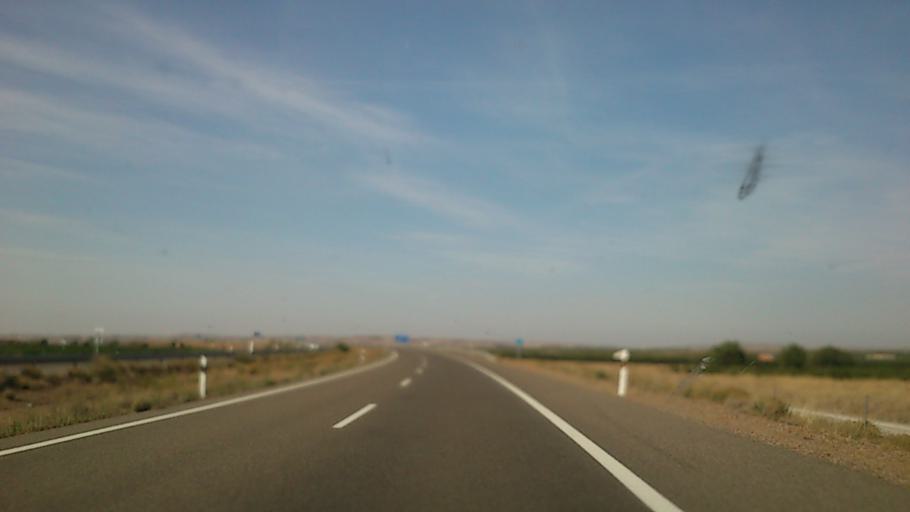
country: ES
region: Aragon
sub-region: Provincia de Zaragoza
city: Carinena
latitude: 41.3546
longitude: -1.2045
